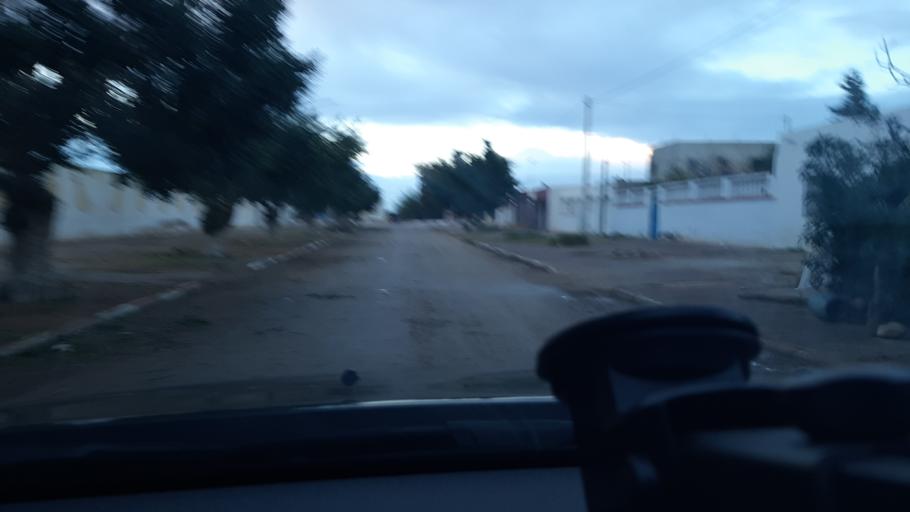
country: TN
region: Al Mahdiyah
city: Shurban
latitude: 34.9661
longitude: 10.3692
